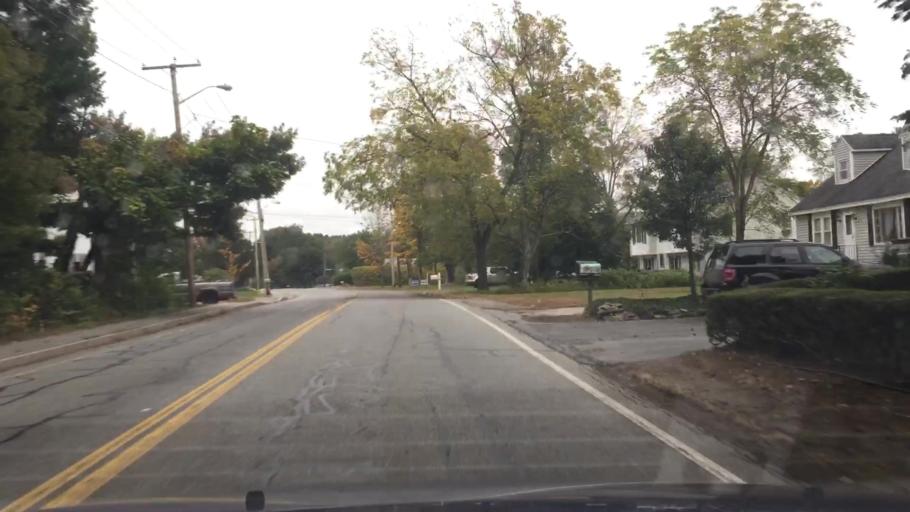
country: US
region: Massachusetts
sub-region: Middlesex County
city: Dracut
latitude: 42.6729
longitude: -71.3575
